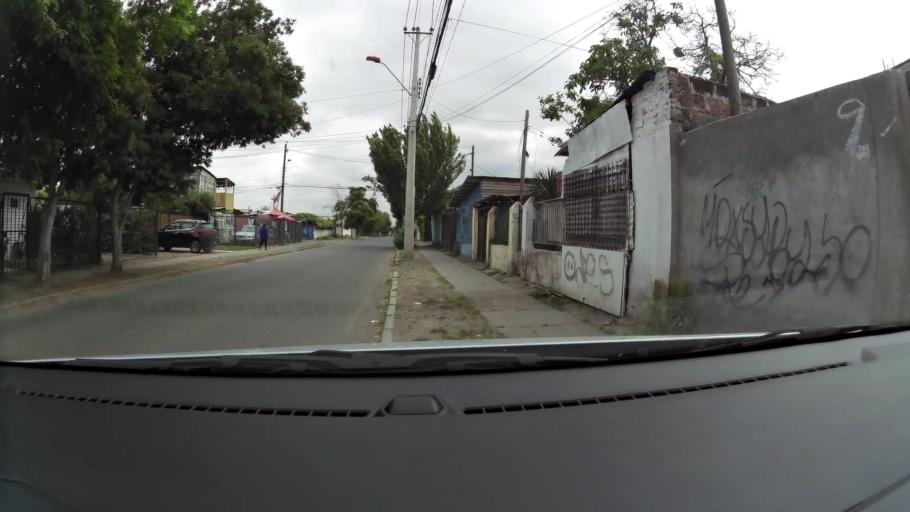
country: CL
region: Santiago Metropolitan
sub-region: Provincia de Santiago
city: Santiago
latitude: -33.5032
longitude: -70.6883
